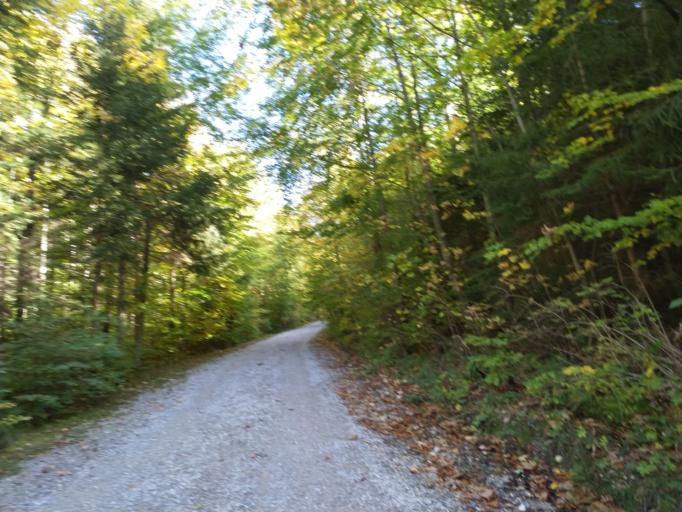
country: AT
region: Tyrol
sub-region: Politischer Bezirk Reutte
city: Vils
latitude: 47.5681
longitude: 10.6553
